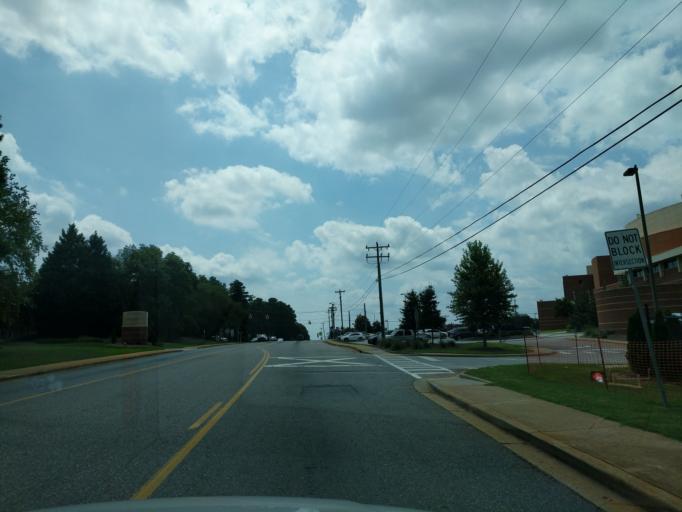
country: US
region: South Carolina
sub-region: Spartanburg County
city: Lyman
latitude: 34.9325
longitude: -82.1256
